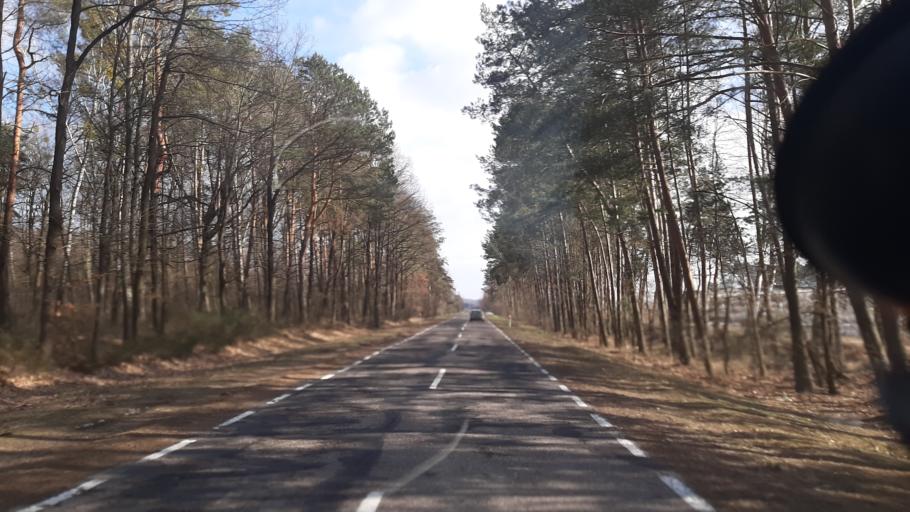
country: PL
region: Lublin Voivodeship
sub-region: Powiat parczewski
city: Sosnowica
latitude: 51.5033
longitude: 23.1366
